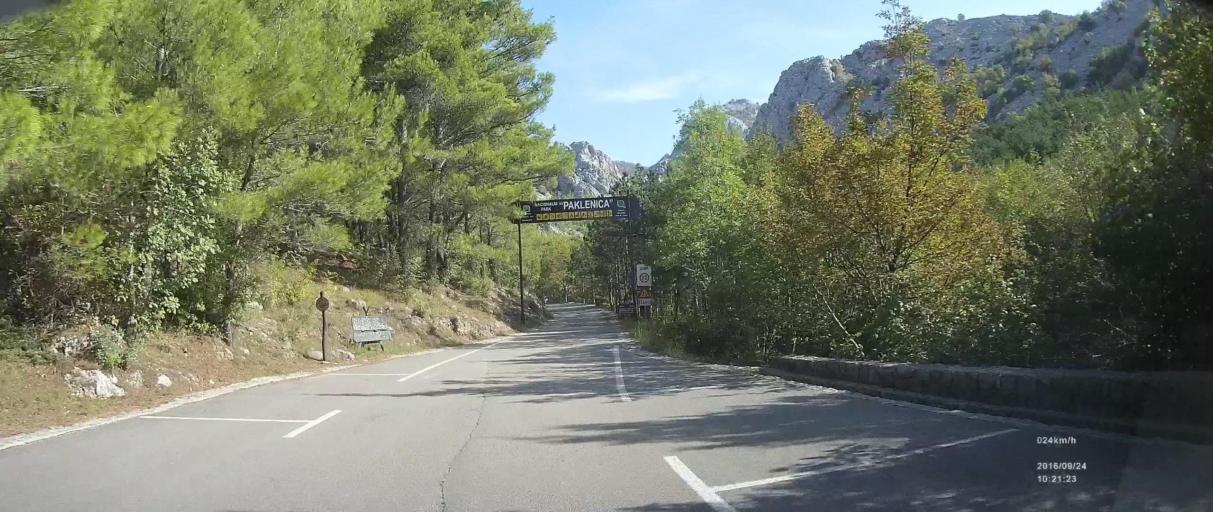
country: HR
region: Zadarska
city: Starigrad
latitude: 44.2947
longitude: 15.4580
